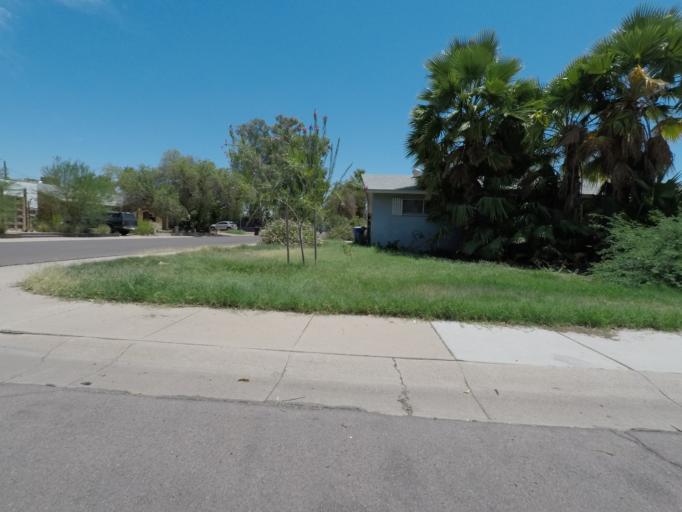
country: US
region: Arizona
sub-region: Maricopa County
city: Tempe Junction
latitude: 33.4160
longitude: -111.9457
